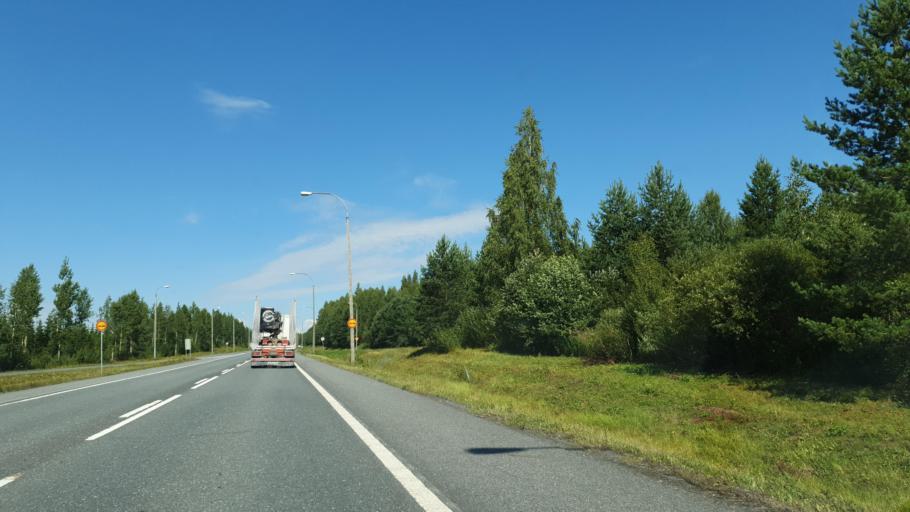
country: FI
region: Northern Savo
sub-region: Ylae-Savo
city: Iisalmi
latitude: 63.5928
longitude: 27.2222
